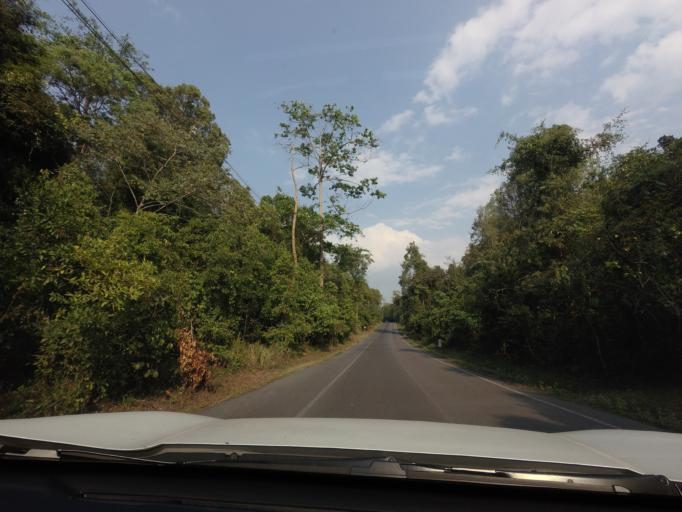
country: TH
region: Nakhon Nayok
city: Nakhon Nayok
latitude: 14.4191
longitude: 101.3808
